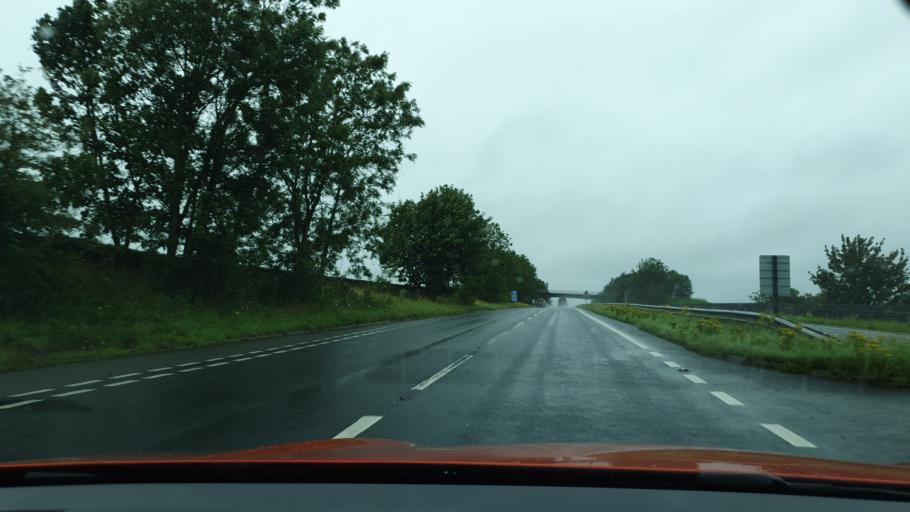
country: GB
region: England
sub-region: Cumbria
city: Grange-over-Sands
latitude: 54.2232
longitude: -2.9064
